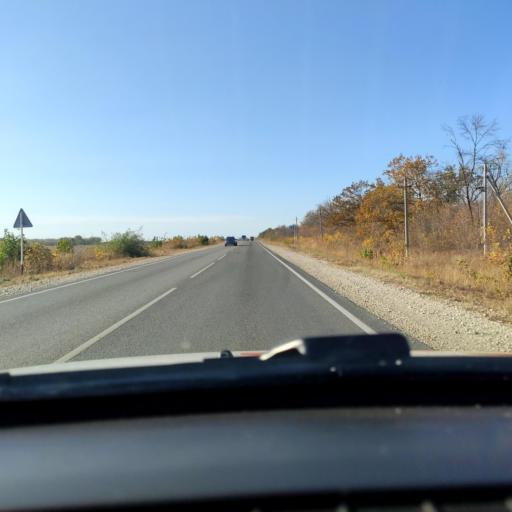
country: RU
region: Voronezj
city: Semiluki
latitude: 51.7291
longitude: 38.9818
